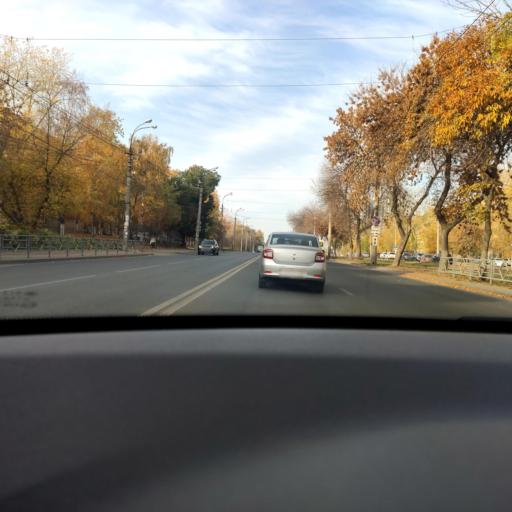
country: RU
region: Samara
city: Samara
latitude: 53.2123
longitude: 50.2097
